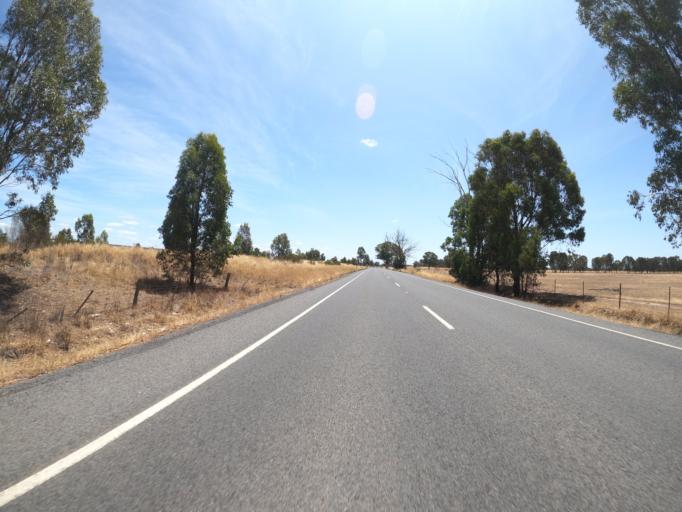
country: AU
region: Victoria
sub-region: Benalla
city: Benalla
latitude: -36.5215
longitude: 146.0355
